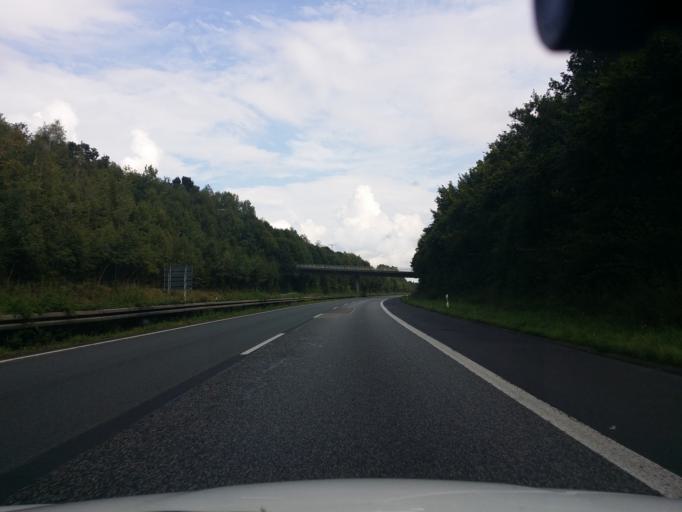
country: DE
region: Hesse
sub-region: Regierungsbezirk Darmstadt
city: Wachtersbach
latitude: 50.2425
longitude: 9.3090
